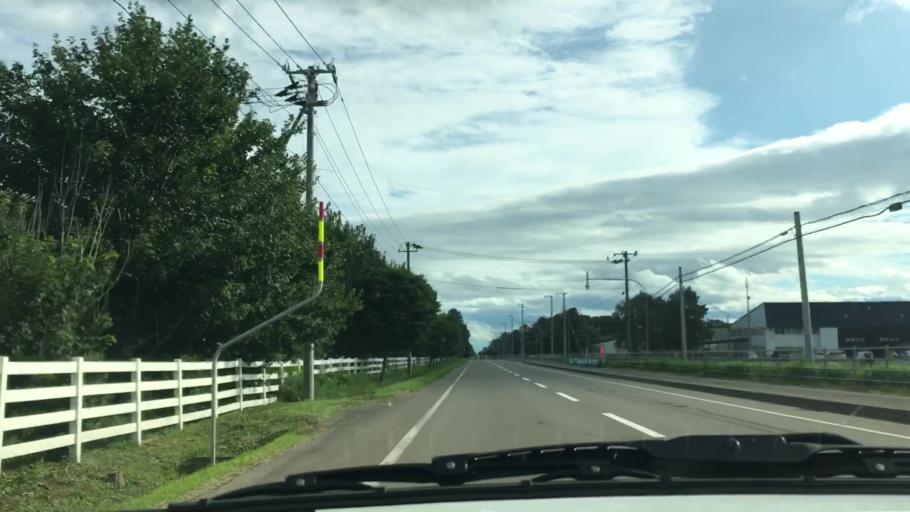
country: JP
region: Hokkaido
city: Otofuke
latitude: 43.2516
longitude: 143.2994
